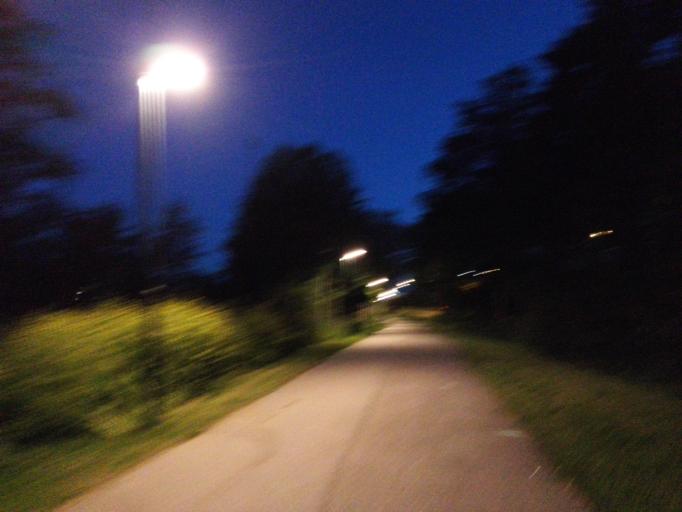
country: SE
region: Stockholm
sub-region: Huddinge Kommun
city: Segeltorp
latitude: 59.2889
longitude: 17.9606
